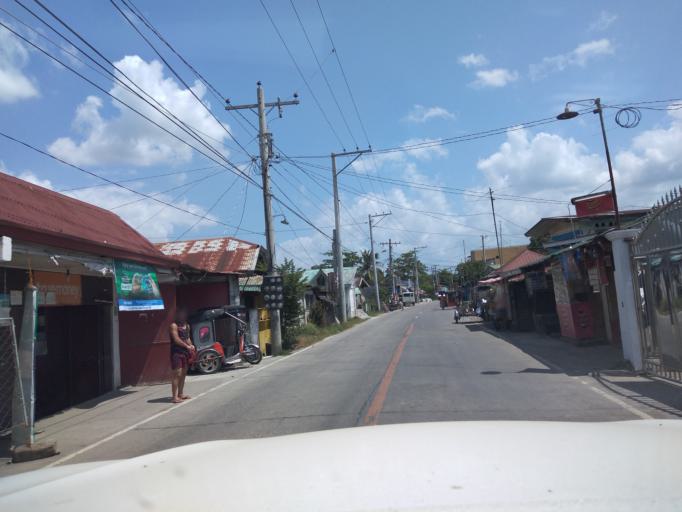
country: PH
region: Central Luzon
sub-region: Province of Pampanga
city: Lourdes
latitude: 15.0195
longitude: 120.8633
